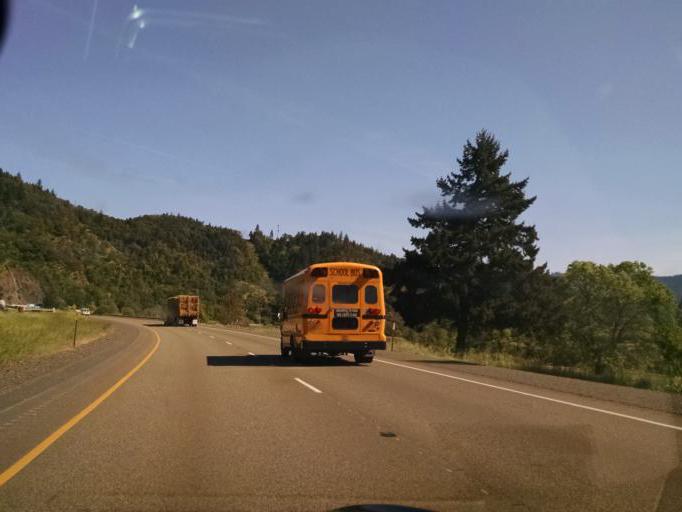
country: US
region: Oregon
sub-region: Douglas County
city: Tri-City
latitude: 42.9641
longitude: -123.3333
